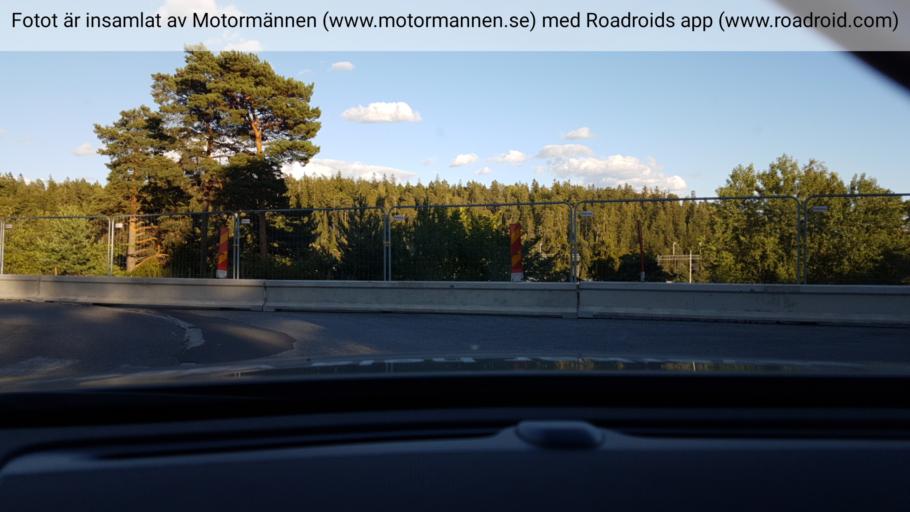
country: SE
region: Stockholm
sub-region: Upplands-Bro Kommun
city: Kungsaengen
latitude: 59.4807
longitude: 17.7574
